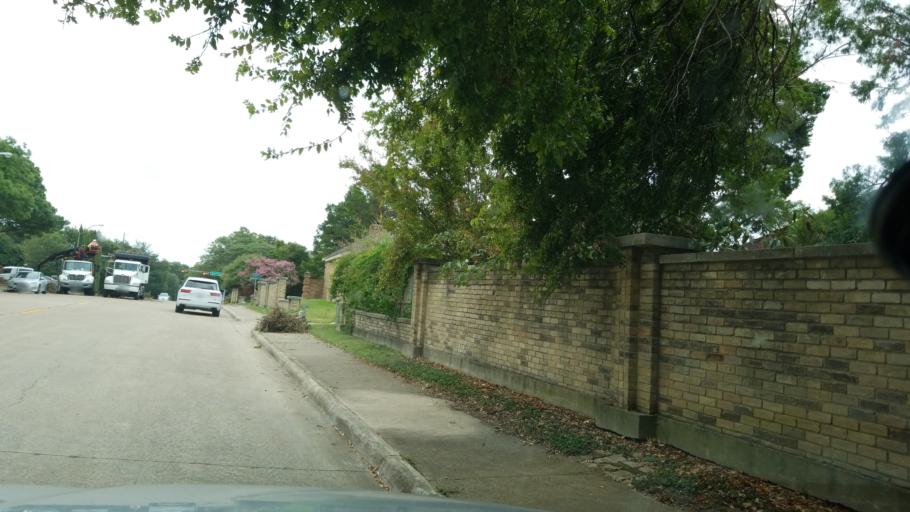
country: US
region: Texas
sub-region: Dallas County
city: Richardson
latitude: 32.8925
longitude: -96.7192
